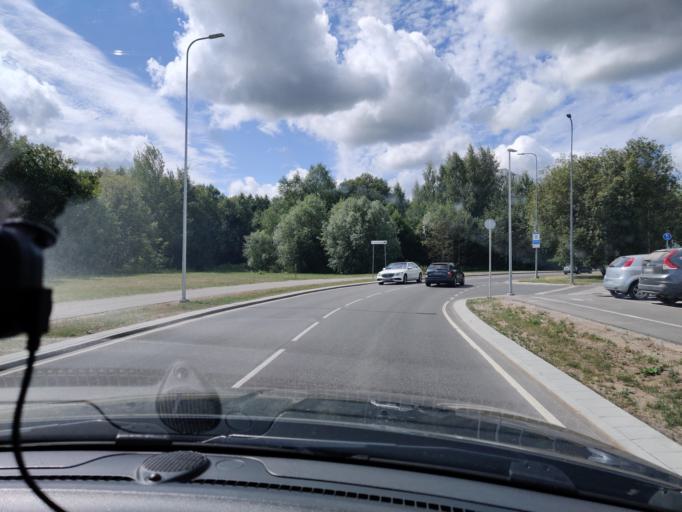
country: EE
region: Harju
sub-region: Saue vald
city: Laagri
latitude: 59.3947
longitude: 24.6564
